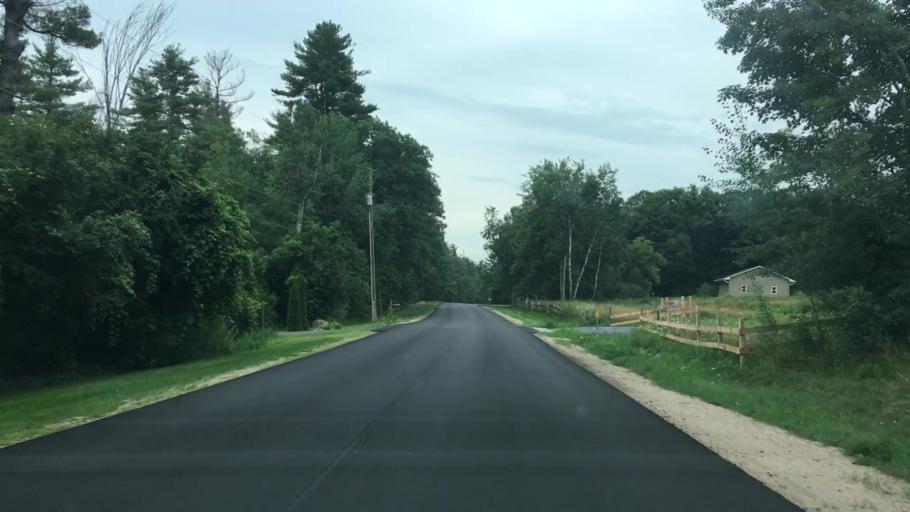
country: US
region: New York
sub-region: Clinton County
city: Peru
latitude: 44.5526
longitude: -73.5655
